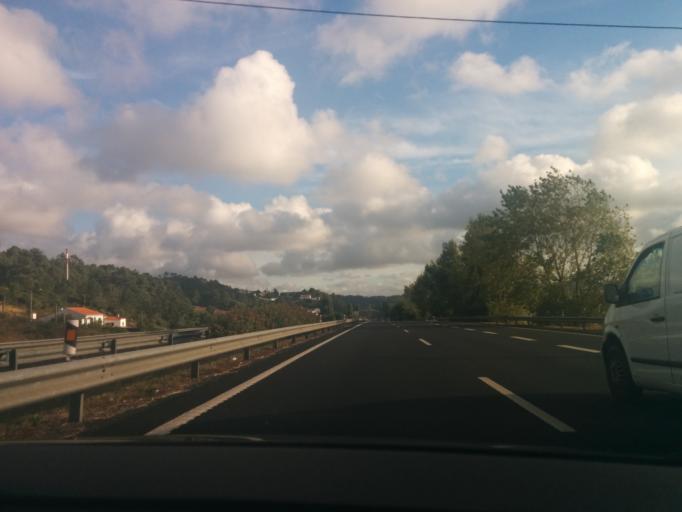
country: PT
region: Leiria
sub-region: Obidos
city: Obidos
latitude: 39.3309
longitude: -9.1746
